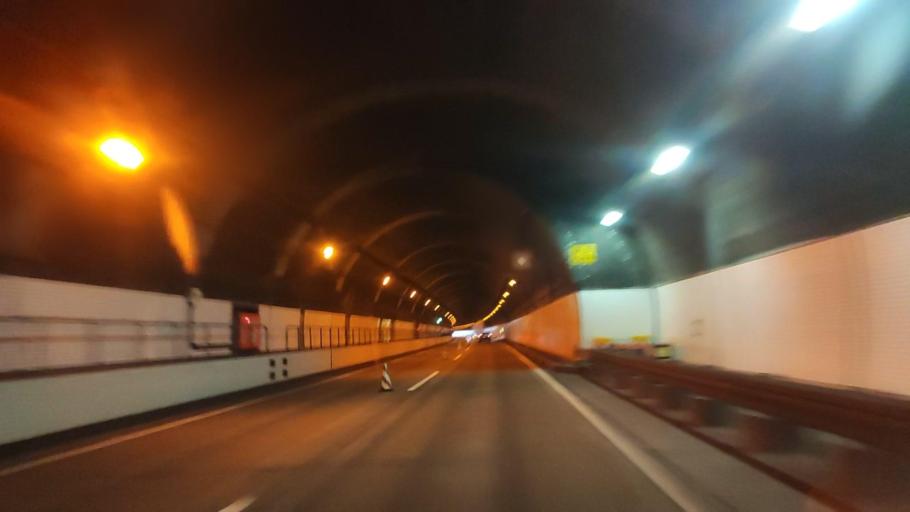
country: JP
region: Niigata
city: Joetsu
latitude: 37.1067
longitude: 138.0433
